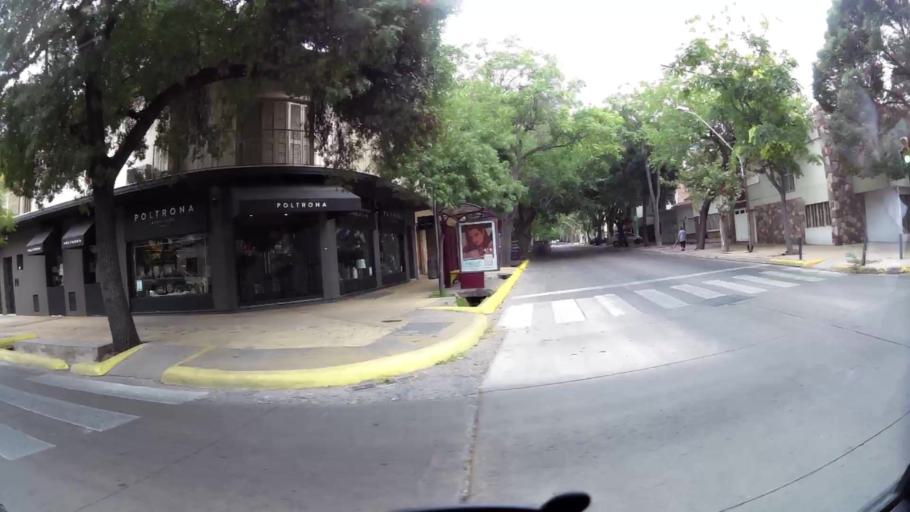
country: AR
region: Mendoza
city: Mendoza
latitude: -32.8904
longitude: -68.8590
